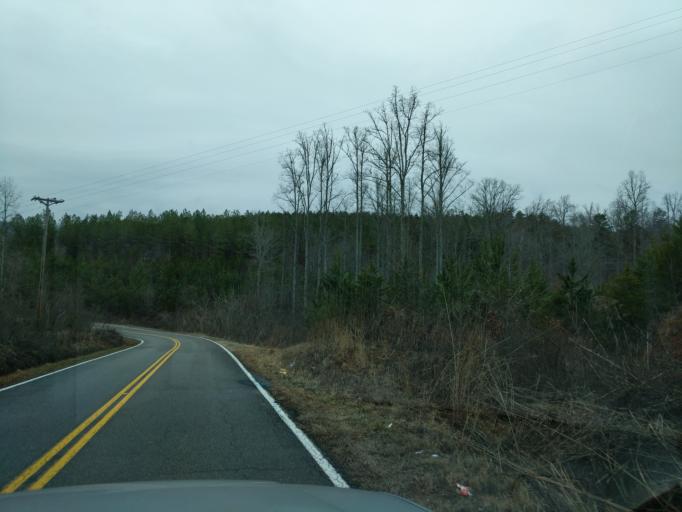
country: US
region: South Carolina
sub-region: Oconee County
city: Walhalla
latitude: 34.7927
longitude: -83.0883
